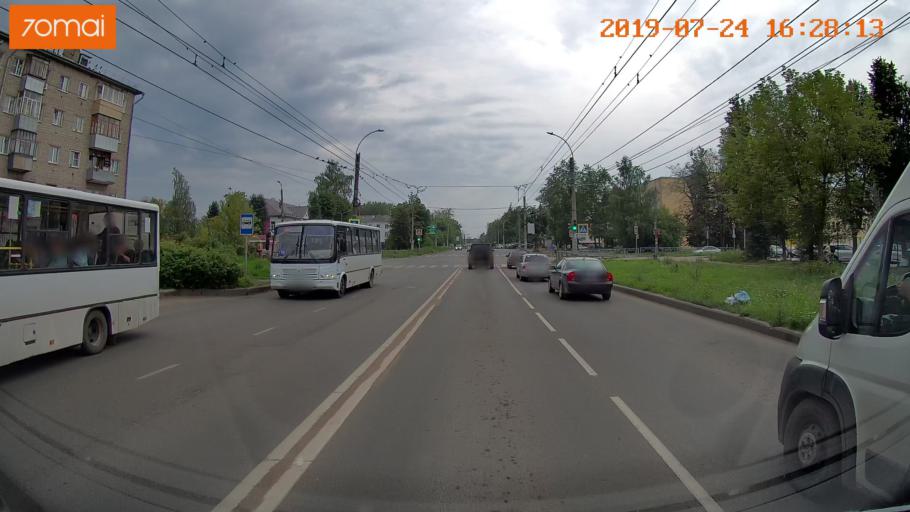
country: RU
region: Ivanovo
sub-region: Gorod Ivanovo
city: Ivanovo
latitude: 56.9730
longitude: 40.9646
